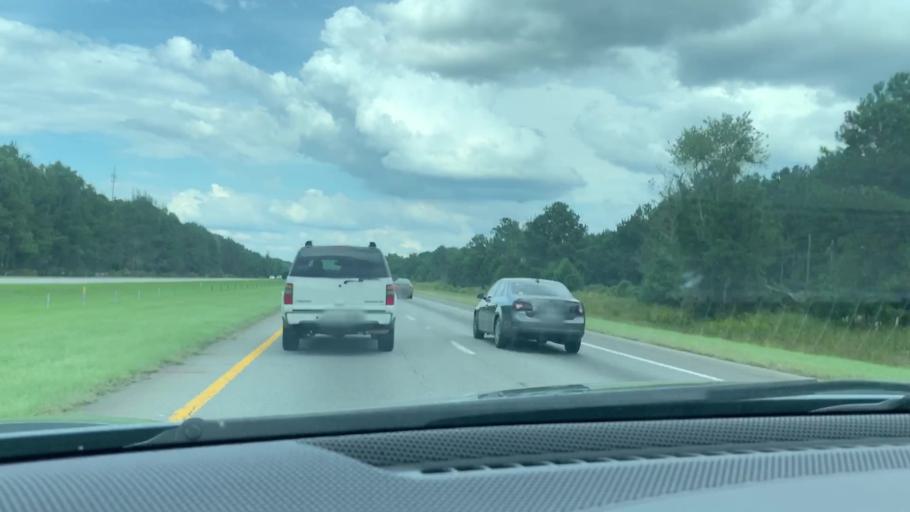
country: US
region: South Carolina
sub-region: Hampton County
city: Yemassee
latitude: 32.6085
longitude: -80.8962
